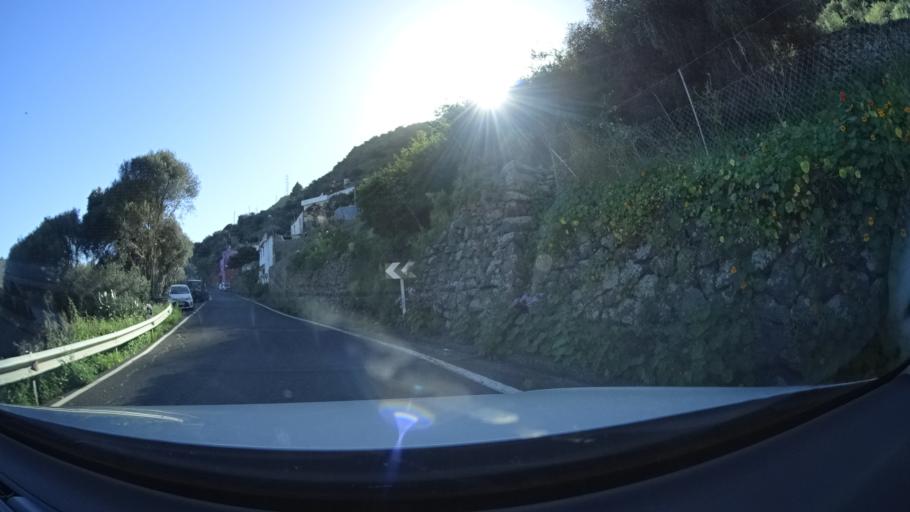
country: ES
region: Canary Islands
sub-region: Provincia de Las Palmas
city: Santa Brigida
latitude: 28.0192
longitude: -15.4740
